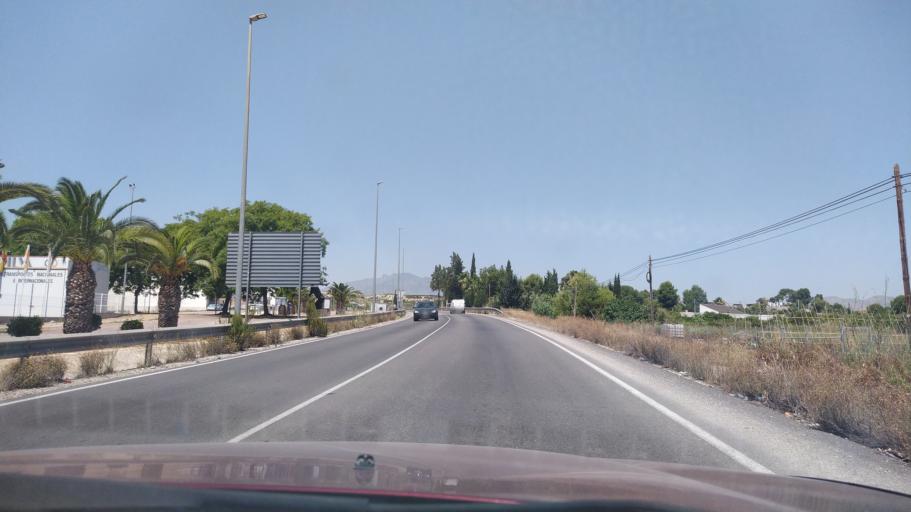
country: ES
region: Murcia
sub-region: Murcia
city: Ceuti
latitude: 38.0869
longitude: -1.2698
